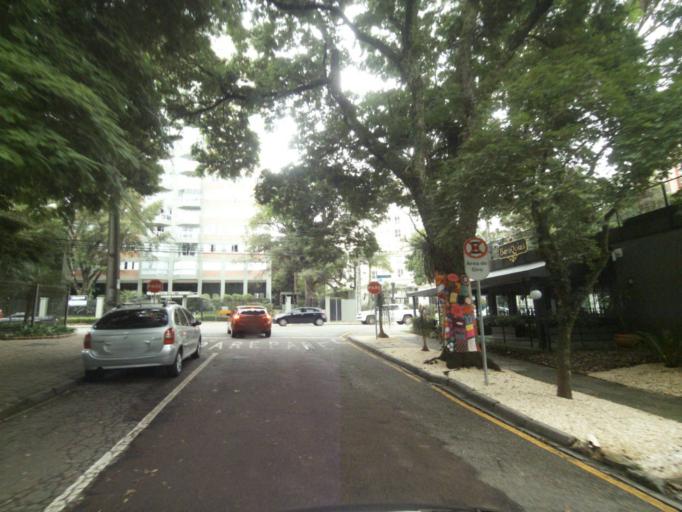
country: BR
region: Parana
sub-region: Curitiba
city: Curitiba
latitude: -25.4110
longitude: -49.2591
